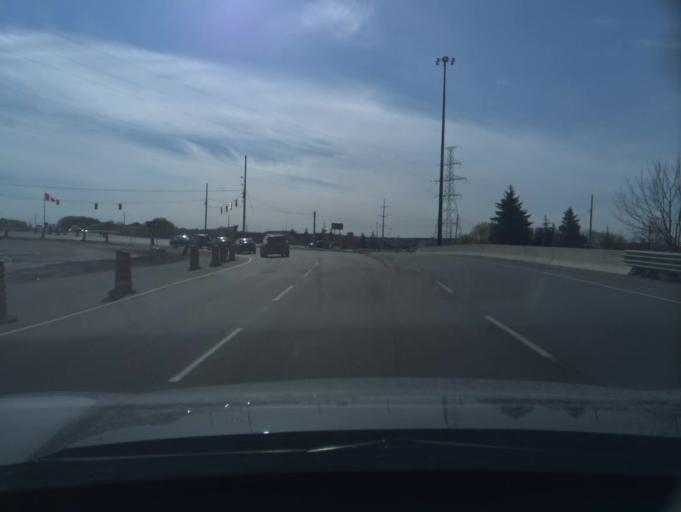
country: CA
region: Ontario
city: North Perth
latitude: 43.8254
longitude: -80.9998
